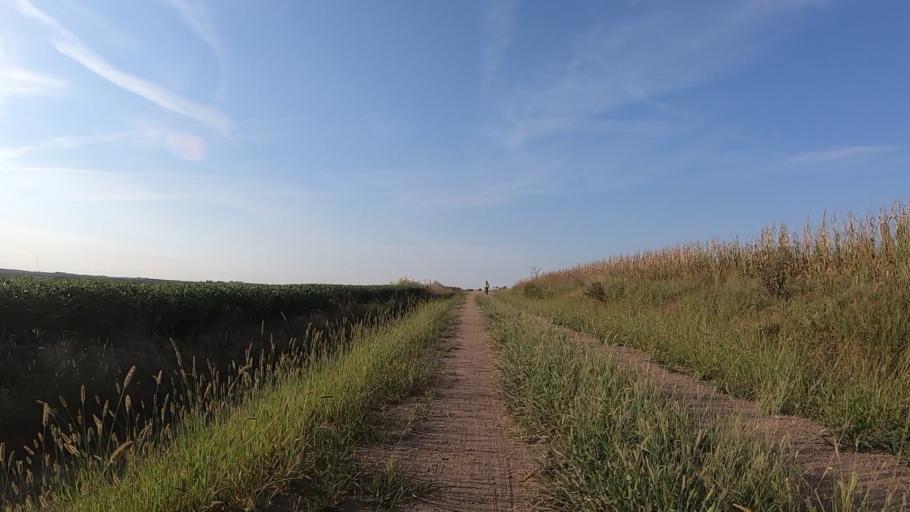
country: US
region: Kansas
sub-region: Marshall County
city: Blue Rapids
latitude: 39.6978
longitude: -96.7792
